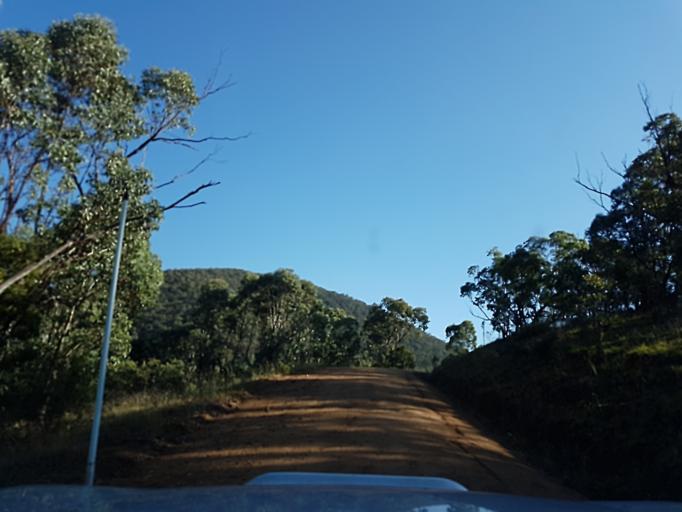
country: AU
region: New South Wales
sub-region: Snowy River
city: Jindabyne
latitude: -36.9371
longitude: 148.3384
